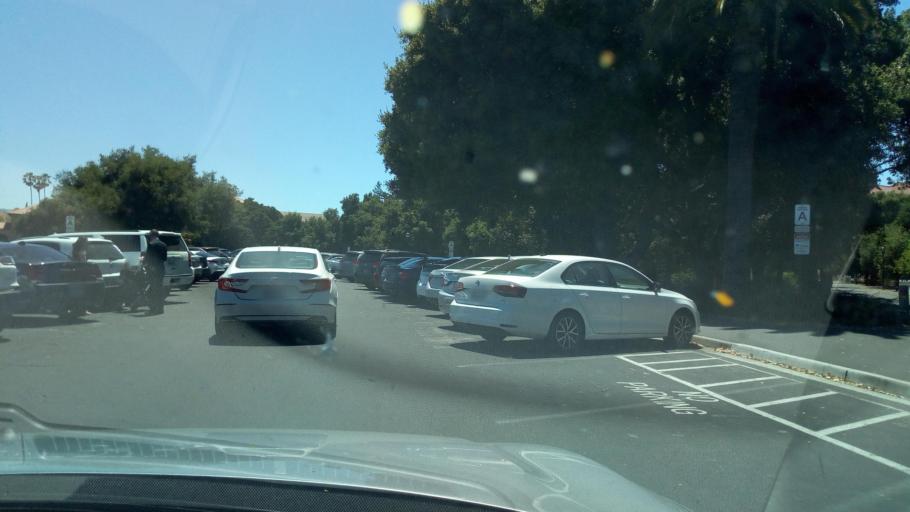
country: US
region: California
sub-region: Santa Clara County
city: Stanford
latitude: 37.4309
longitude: -122.1696
